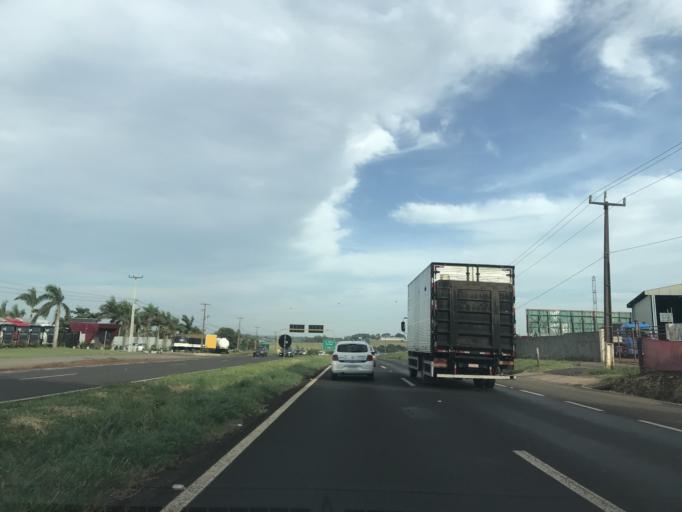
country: BR
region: Parana
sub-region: Maringa
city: Maringa
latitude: -23.3995
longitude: -52.0013
